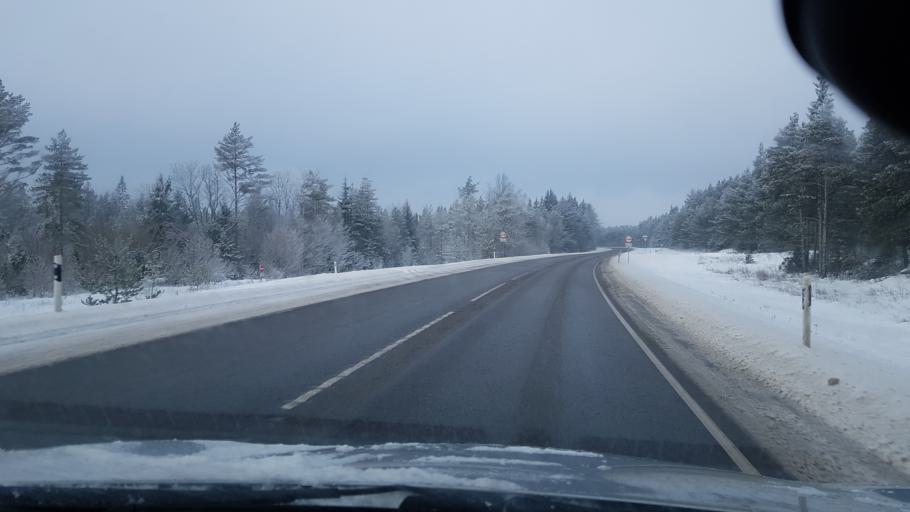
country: EE
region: Harju
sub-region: Keila linn
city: Keila
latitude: 59.3315
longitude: 24.2934
